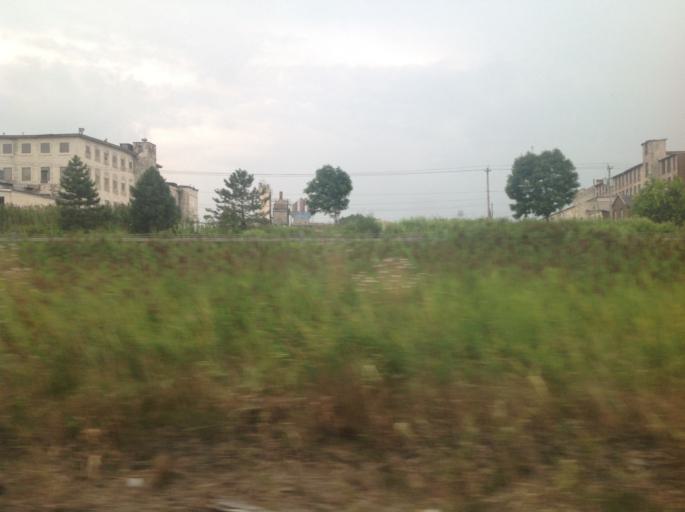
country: US
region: New York
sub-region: Oneida County
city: Utica
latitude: 43.1007
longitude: -75.2107
